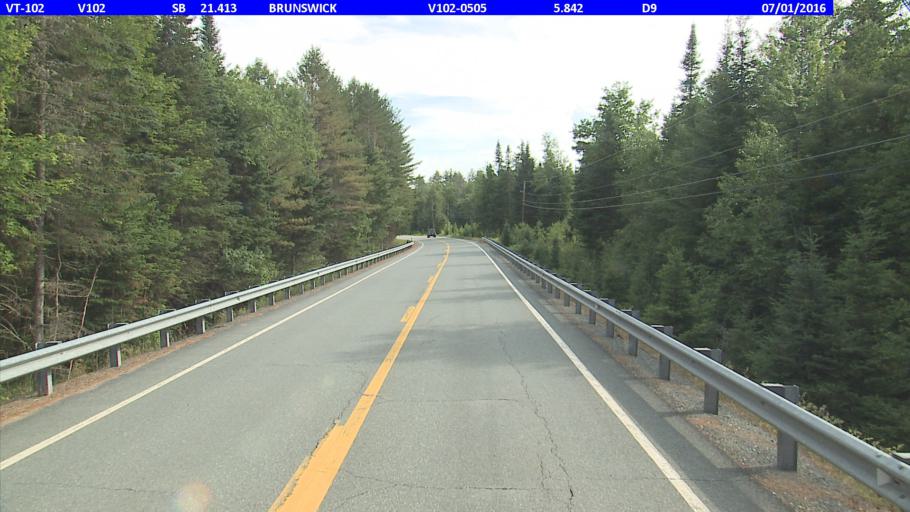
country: US
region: New Hampshire
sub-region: Coos County
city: Stratford
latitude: 44.7318
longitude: -71.6351
